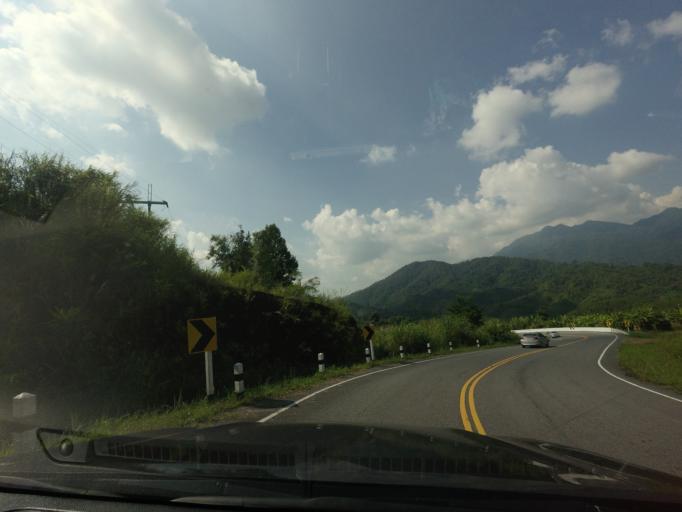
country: TH
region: Nan
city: Santi Suk
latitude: 18.9759
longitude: 101.0109
